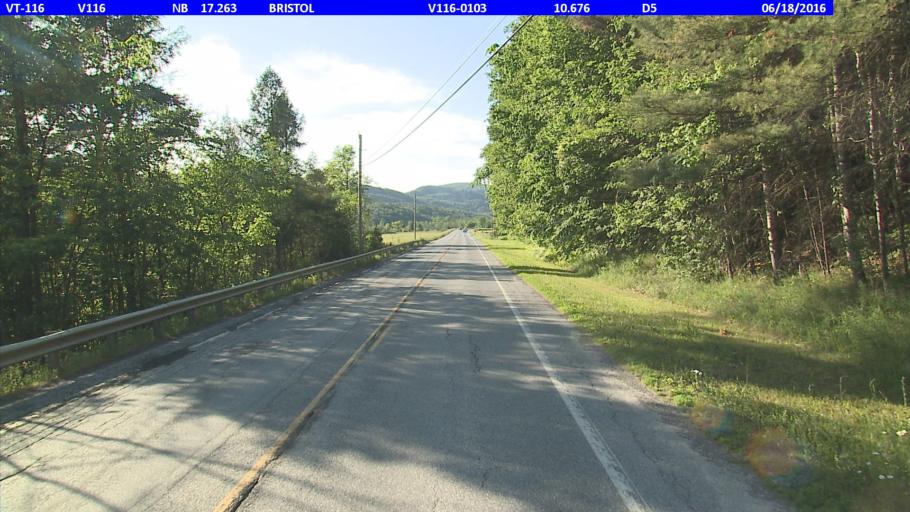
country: US
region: Vermont
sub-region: Addison County
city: Bristol
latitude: 44.1635
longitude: -73.0525
